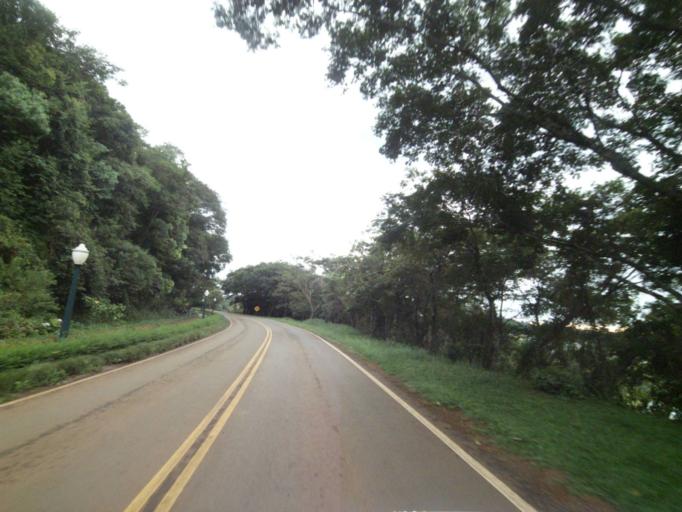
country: BR
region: Parana
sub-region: Guaraniacu
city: Guaraniacu
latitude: -25.1000
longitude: -52.8886
